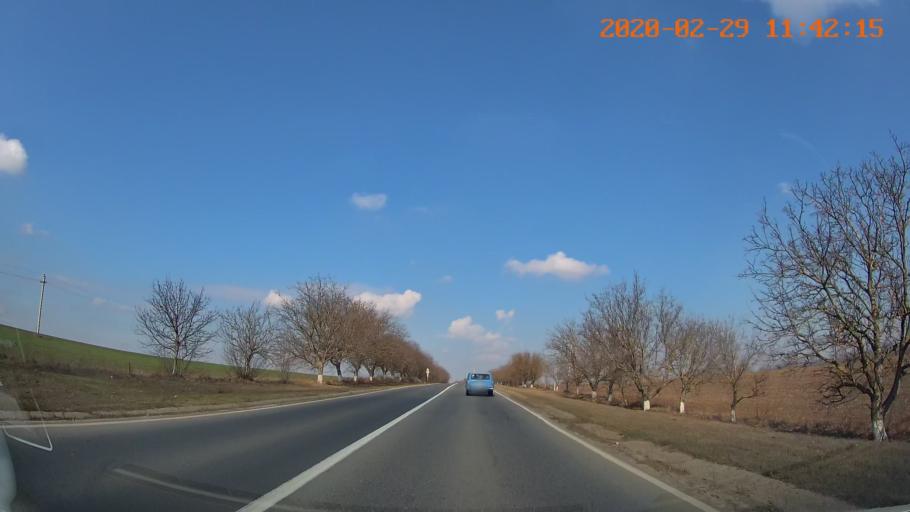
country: MD
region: Rezina
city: Saharna
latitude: 47.6814
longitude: 29.0136
